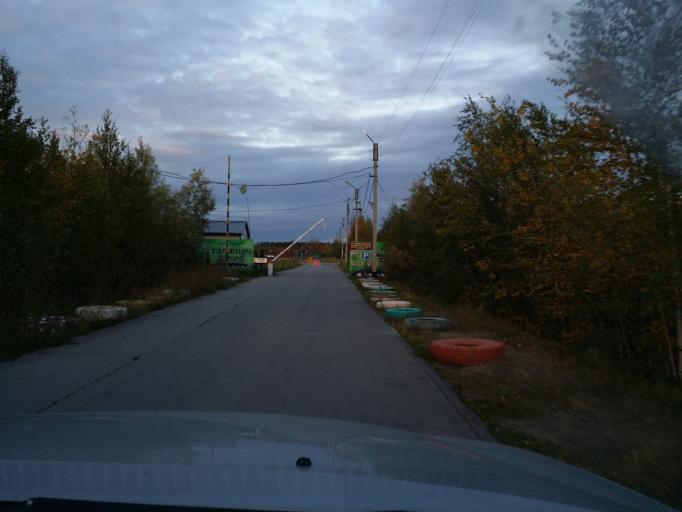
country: RU
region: Khanty-Mansiyskiy Avtonomnyy Okrug
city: Megion
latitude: 61.0834
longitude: 76.1647
